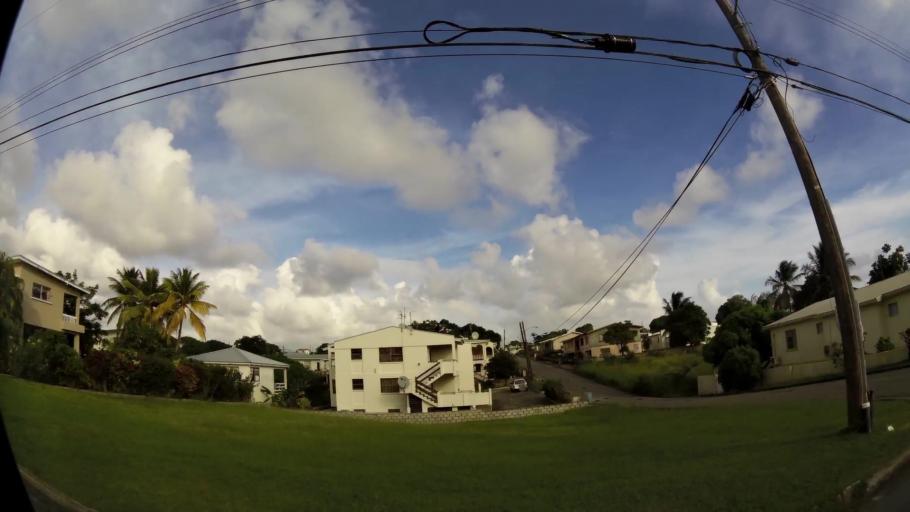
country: BB
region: Christ Church
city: Oistins
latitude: 13.0888
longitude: -59.5706
